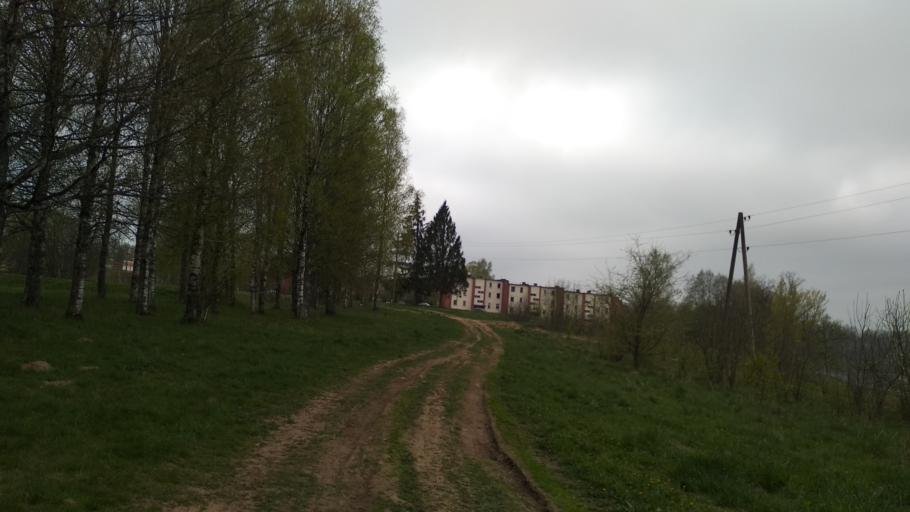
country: LV
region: Malpils
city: Malpils
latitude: 57.0143
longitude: 24.9527
